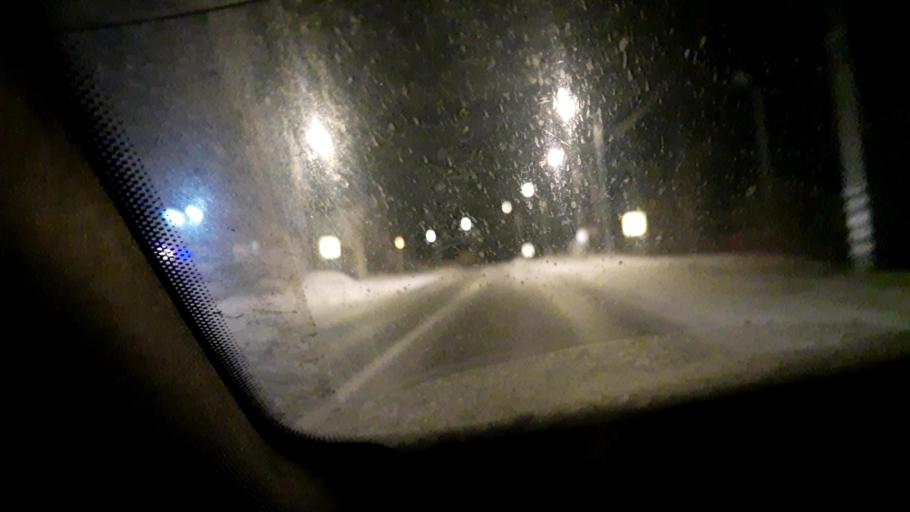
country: RU
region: Moskovskaya
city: Shemetovo
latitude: 56.6755
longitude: 38.1465
